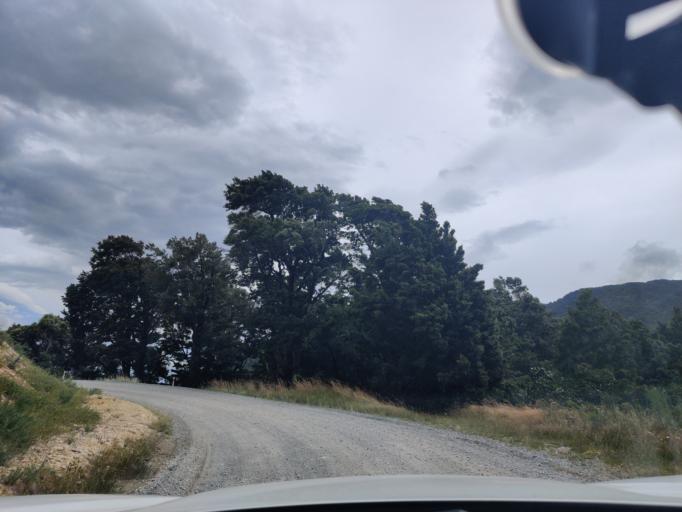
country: NZ
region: Wellington
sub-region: Masterton District
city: Masterton
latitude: -41.0397
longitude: 175.4037
